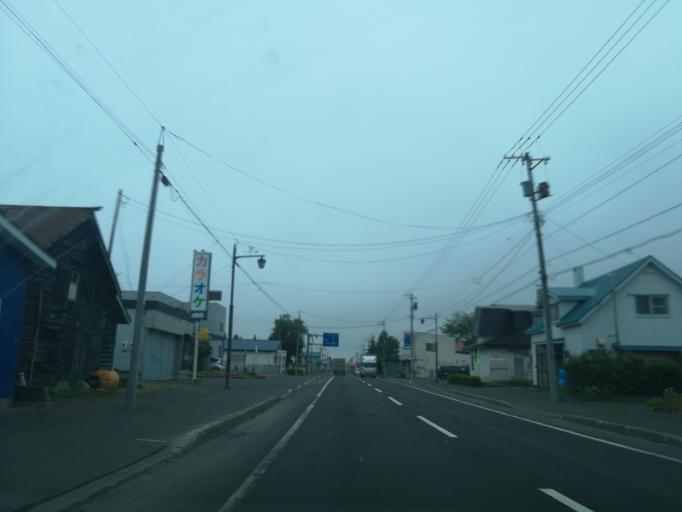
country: JP
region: Hokkaido
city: Ebetsu
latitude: 43.0715
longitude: 141.6478
